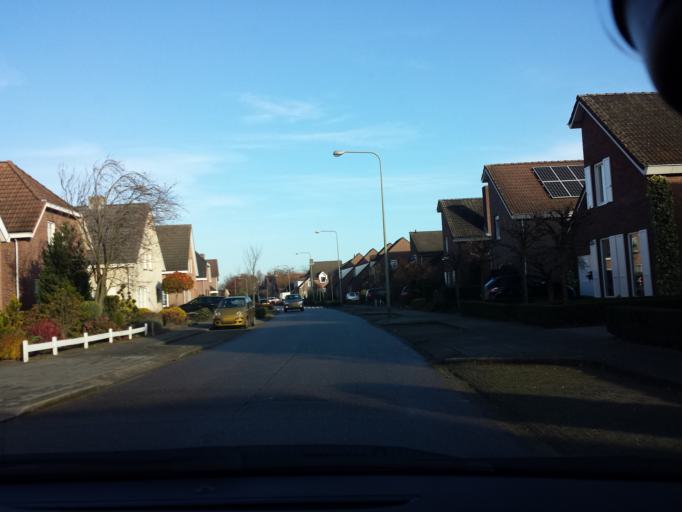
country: NL
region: Limburg
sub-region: Gemeente Maasgouw
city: Maasbracht
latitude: 51.1097
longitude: 5.8790
